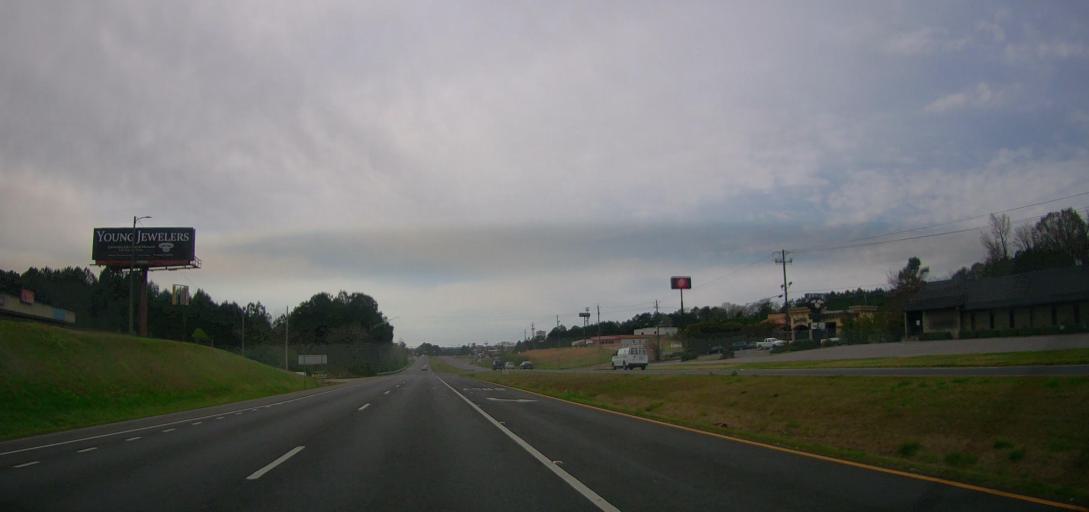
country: US
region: Alabama
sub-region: Walker County
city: Jasper
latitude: 33.8461
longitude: -87.2595
